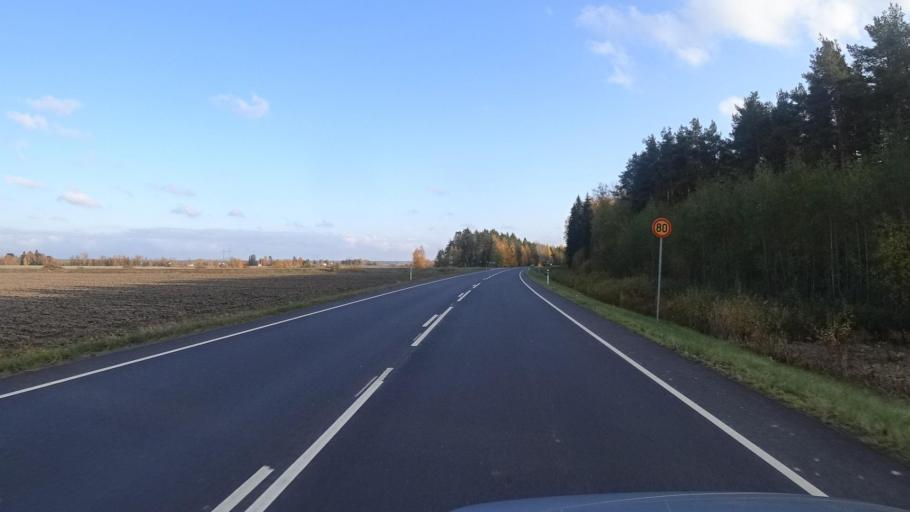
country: FI
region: Satakunta
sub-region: Rauma
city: Saekylae
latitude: 61.0692
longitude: 22.3164
